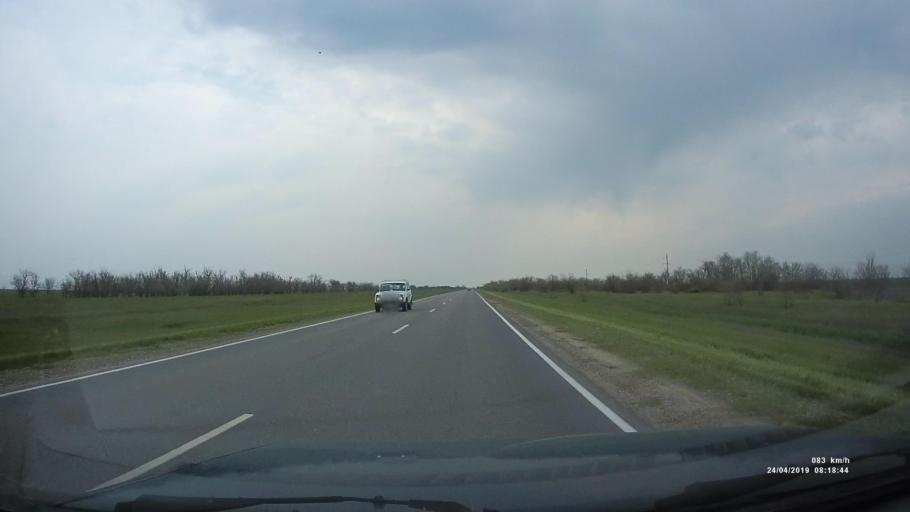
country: RU
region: Kalmykiya
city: Priyutnoye
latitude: 46.1018
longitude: 43.6531
